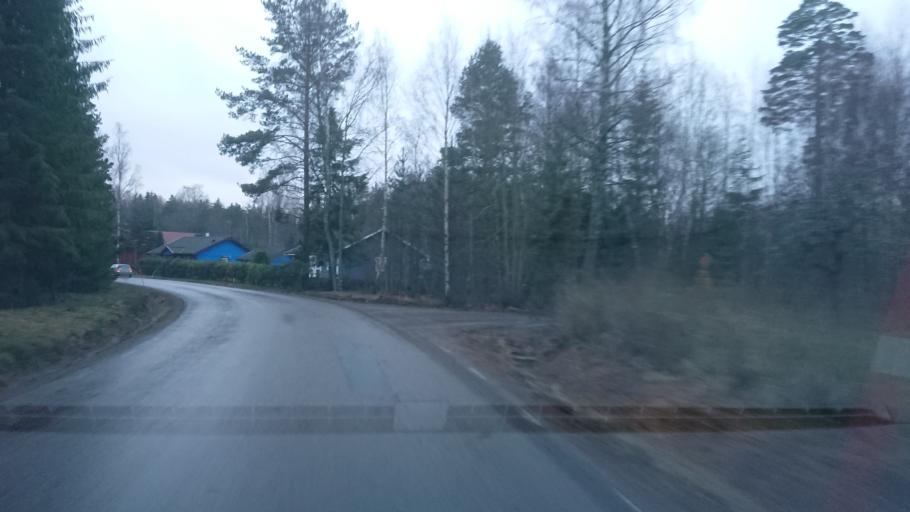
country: SE
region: Uppsala
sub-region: Osthammars Kommun
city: Bjorklinge
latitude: 59.9916
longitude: 17.5914
